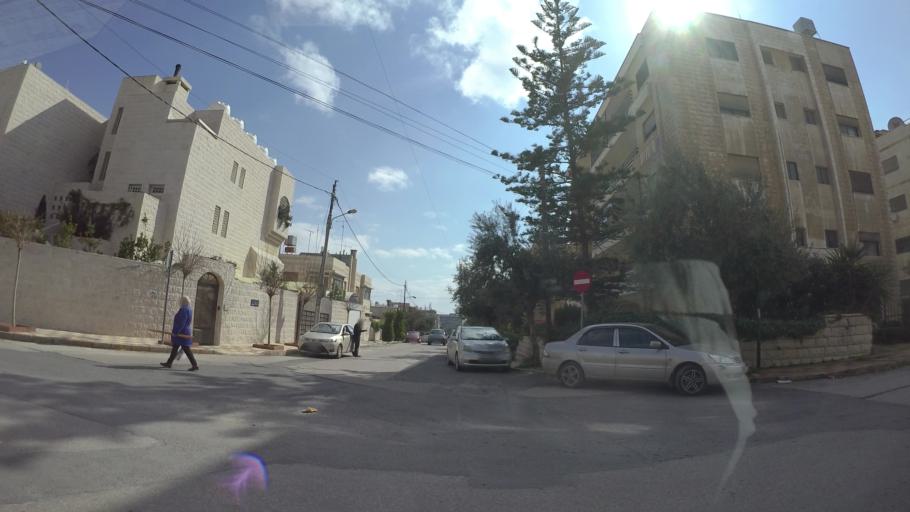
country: JO
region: Amman
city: Amman
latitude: 31.9727
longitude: 35.8941
